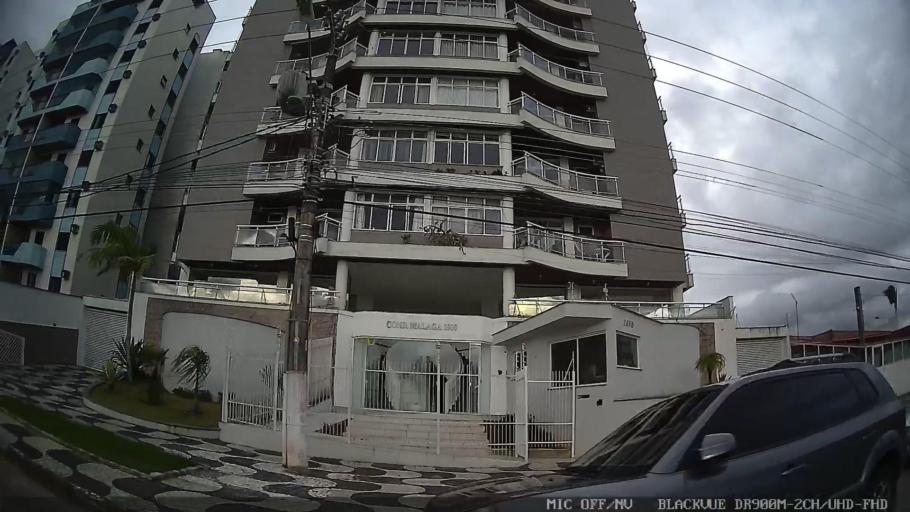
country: BR
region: Sao Paulo
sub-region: Caraguatatuba
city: Caraguatatuba
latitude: -23.6447
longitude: -45.4250
